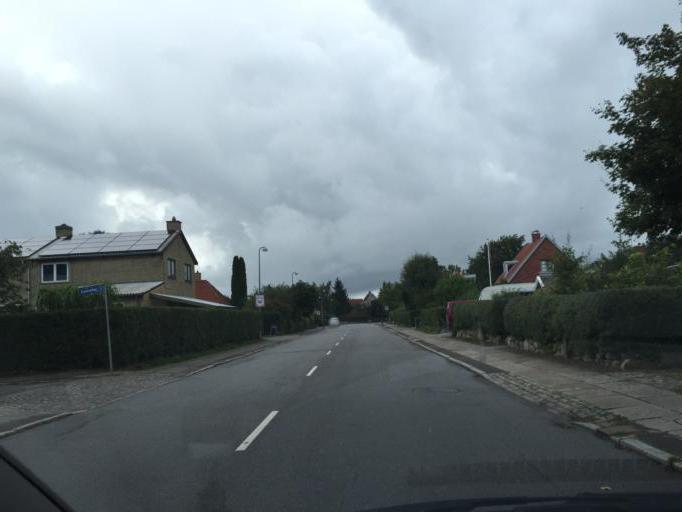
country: DK
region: Capital Region
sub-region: Gladsaxe Municipality
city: Buddinge
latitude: 55.7546
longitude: 12.4713
